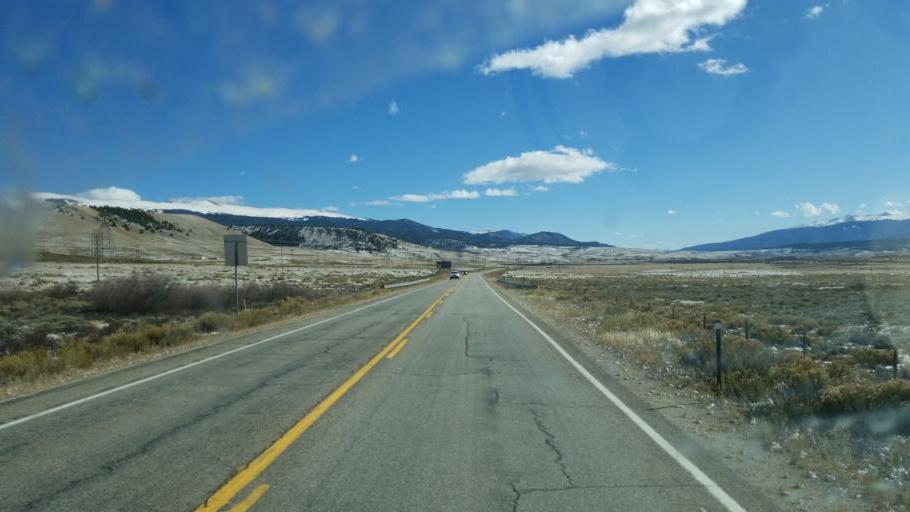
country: US
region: Colorado
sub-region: Lake County
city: Leadville
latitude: 39.1895
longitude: -106.3316
